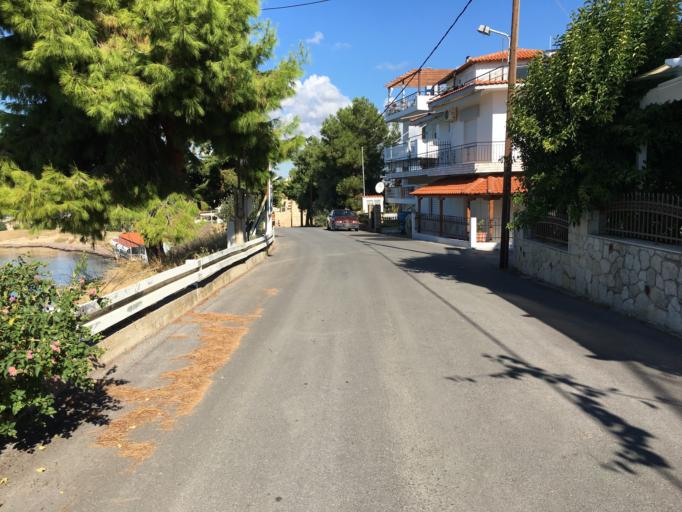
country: GR
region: Central Macedonia
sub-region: Nomos Chalkidikis
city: Nea Poteidaia
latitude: 40.1943
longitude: 23.3249
